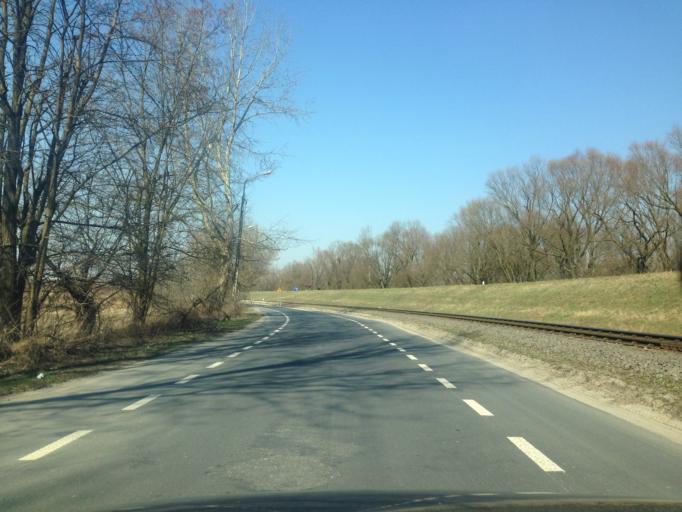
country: PL
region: Masovian Voivodeship
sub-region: Warszawa
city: Wilanow
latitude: 52.1697
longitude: 21.1233
